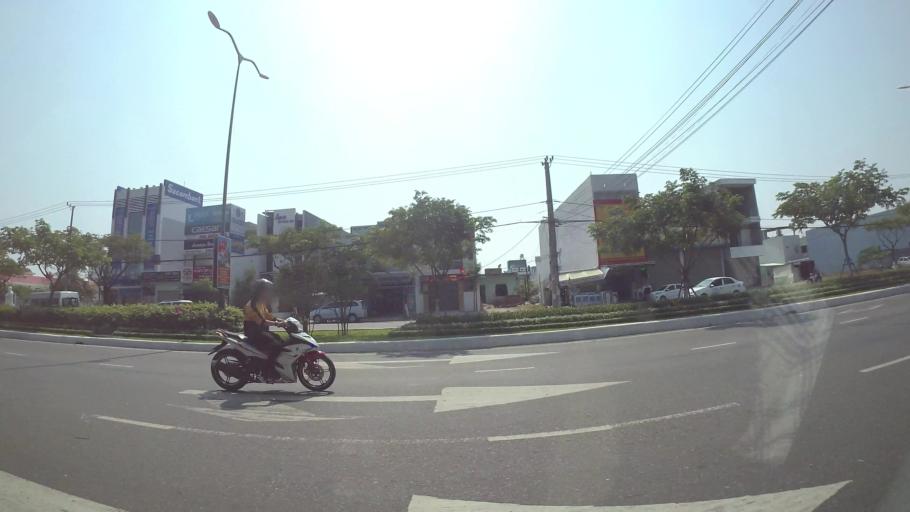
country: VN
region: Da Nang
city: Ngu Hanh Son
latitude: 16.0175
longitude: 108.2538
